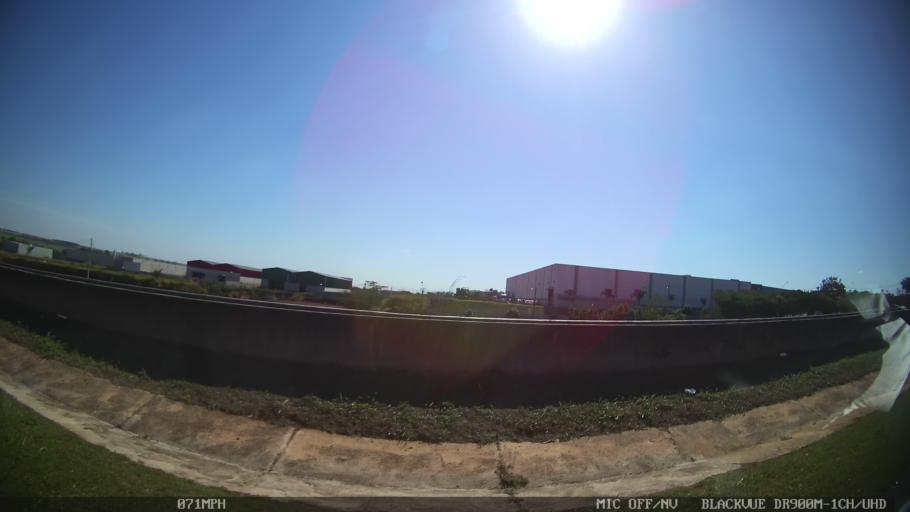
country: BR
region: Sao Paulo
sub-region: Ribeirao Preto
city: Ribeirao Preto
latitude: -21.1006
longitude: -47.7999
